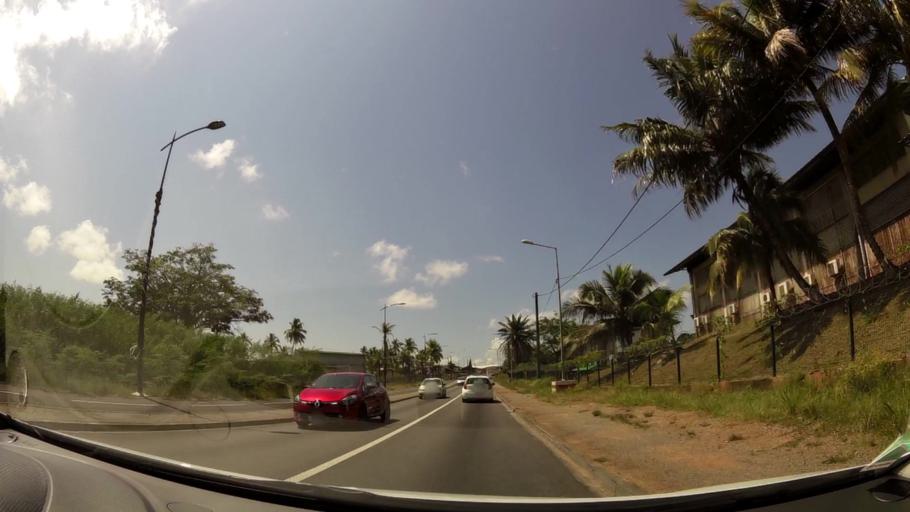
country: GF
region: Guyane
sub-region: Guyane
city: Cayenne
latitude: 4.9229
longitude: -52.3237
